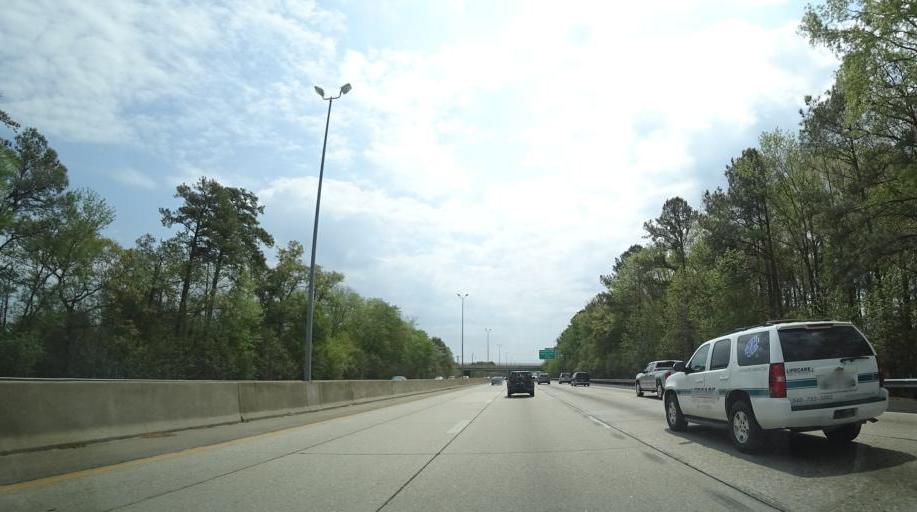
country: US
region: Virginia
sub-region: City of Newport News
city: Newport News
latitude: 37.0674
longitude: -76.4303
